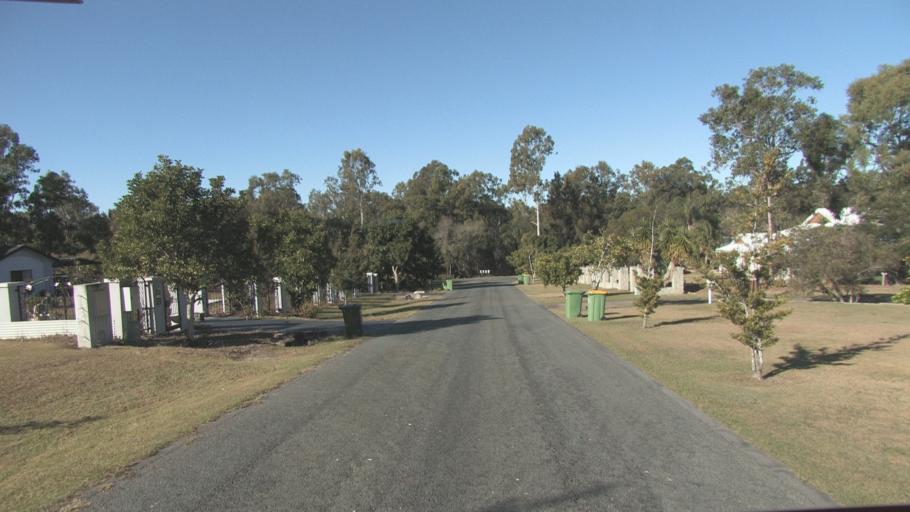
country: AU
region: Queensland
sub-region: Logan
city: North Maclean
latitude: -27.7495
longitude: 152.9588
